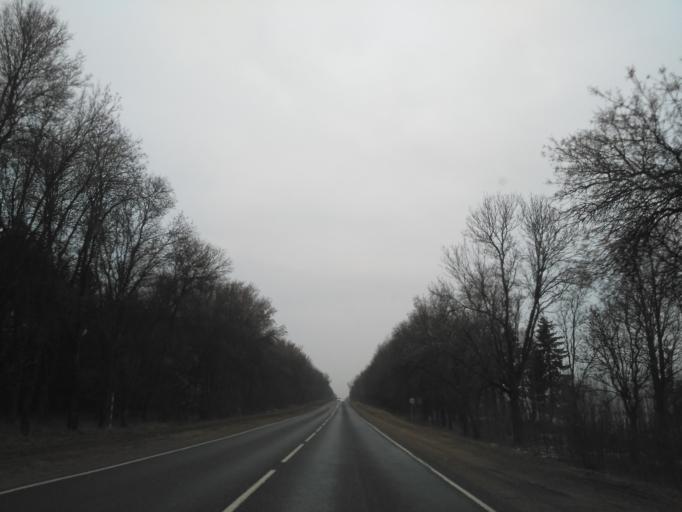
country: BY
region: Minsk
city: Novy Svyerzhan'
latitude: 53.4417
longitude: 26.6593
